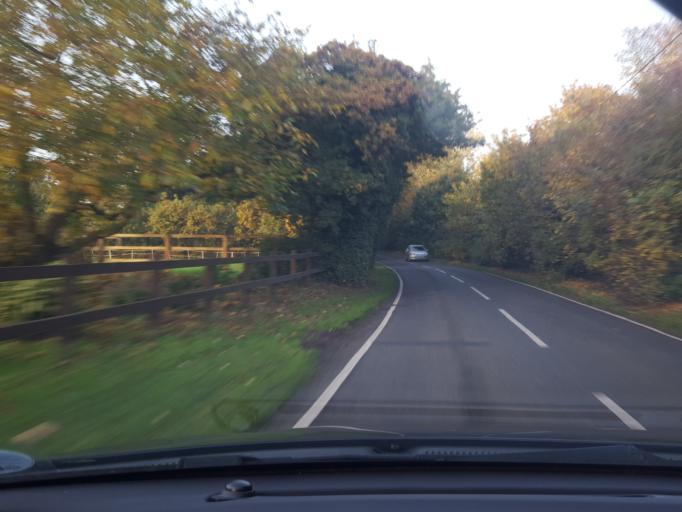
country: GB
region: England
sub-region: Essex
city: Saint Osyth
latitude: 51.8170
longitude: 1.0957
